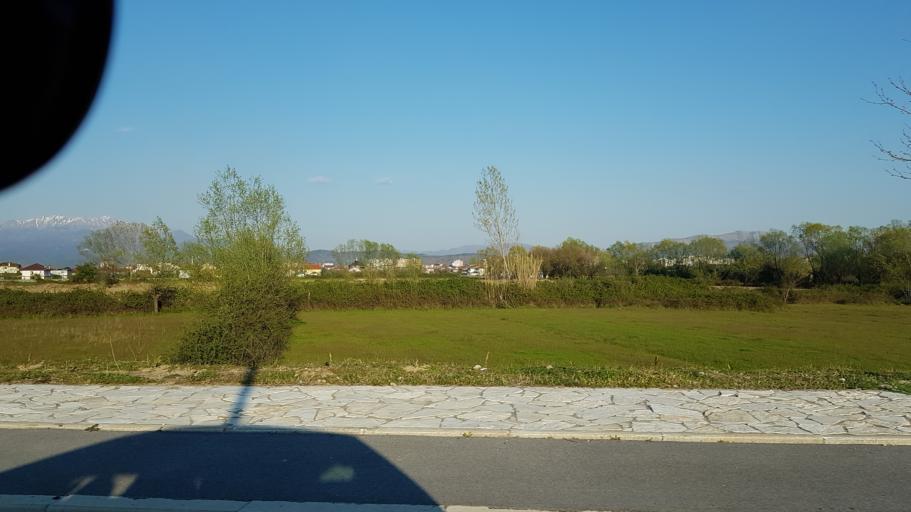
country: AL
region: Shkoder
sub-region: Rrethi i Shkodres
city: Shkoder
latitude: 42.0732
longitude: 19.4897
